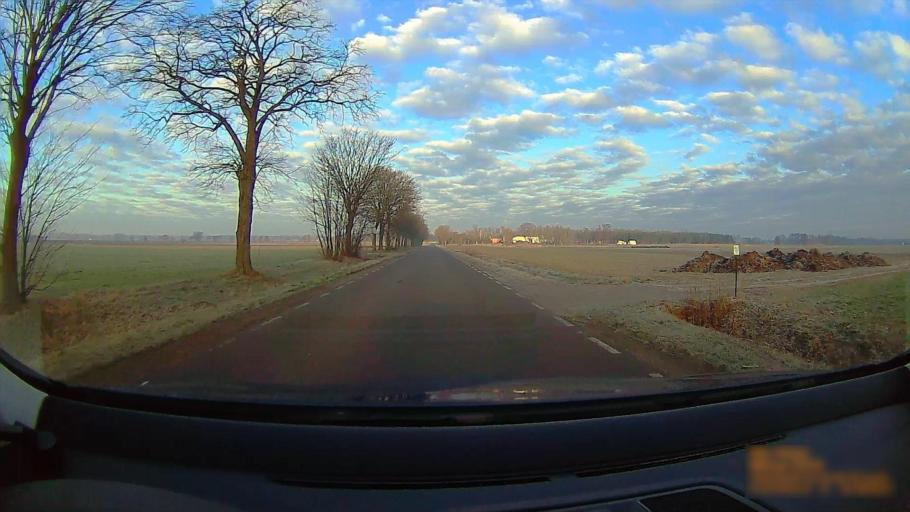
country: PL
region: Greater Poland Voivodeship
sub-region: Powiat koninski
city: Rychwal
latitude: 52.0986
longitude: 18.1080
